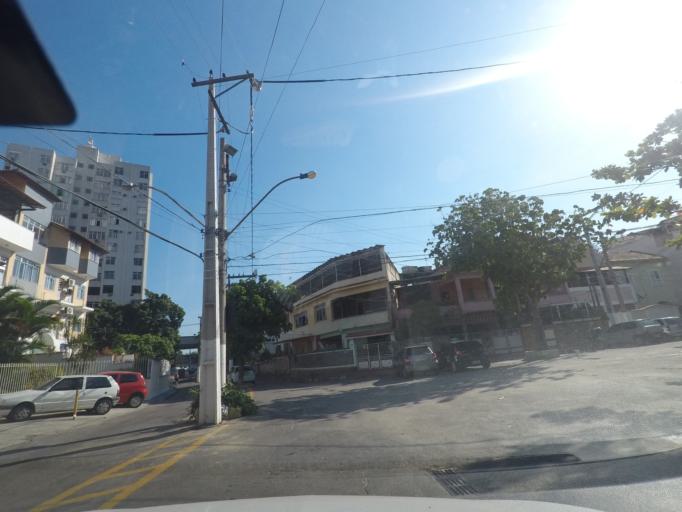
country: BR
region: Rio de Janeiro
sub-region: Niteroi
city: Niteroi
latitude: -22.8836
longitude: -43.1269
